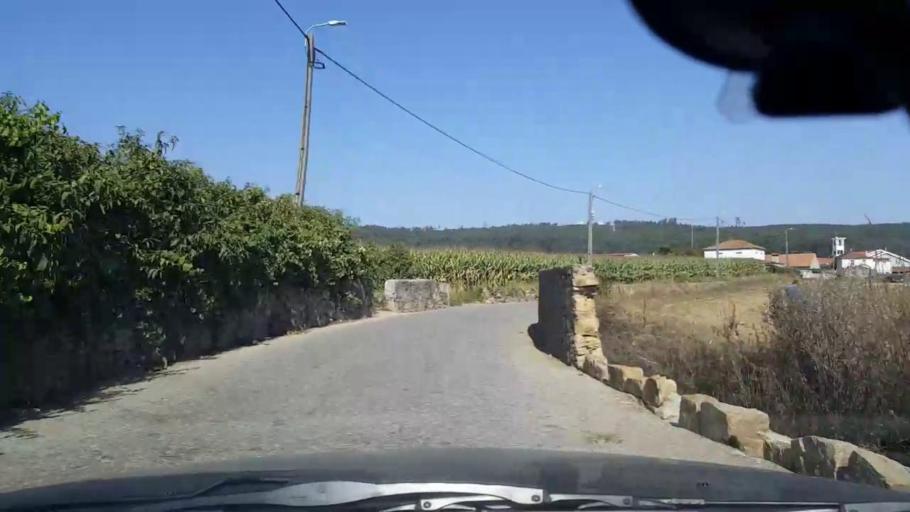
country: PT
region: Porto
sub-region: Povoa de Varzim
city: Pedroso
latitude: 41.4123
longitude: -8.7031
